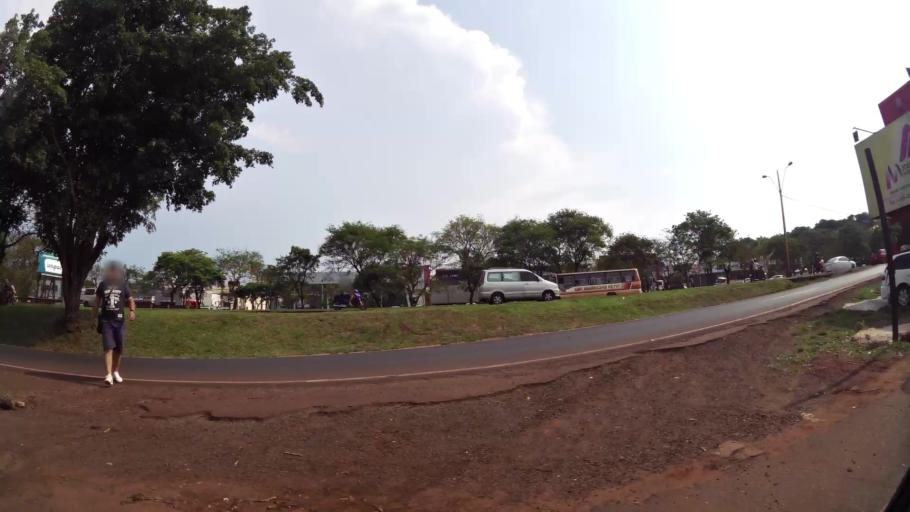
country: PY
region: Alto Parana
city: Ciudad del Este
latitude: -25.5050
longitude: -54.6444
